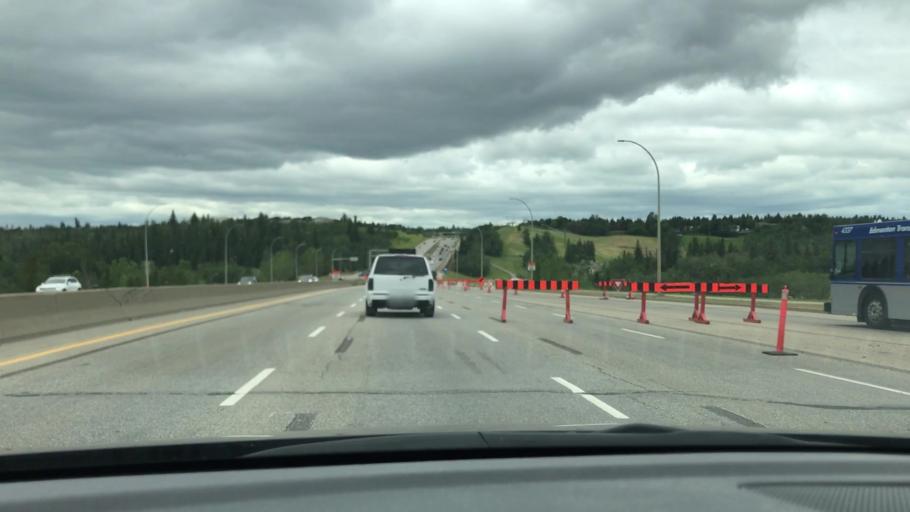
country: CA
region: Alberta
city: Edmonton
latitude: 53.4829
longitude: -113.5469
